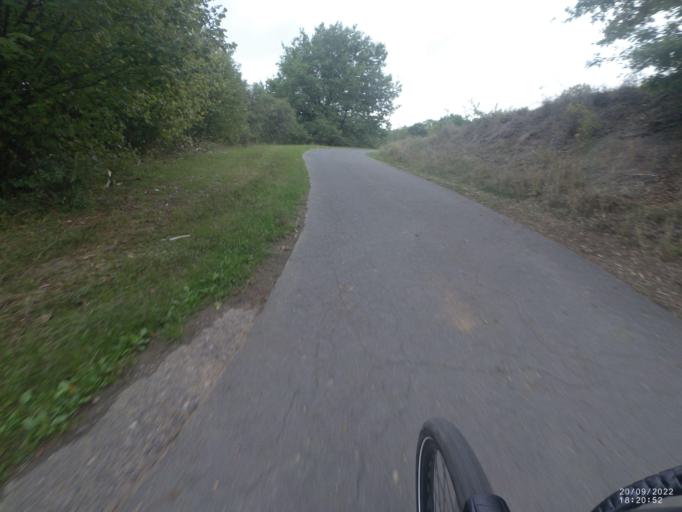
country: DE
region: Rheinland-Pfalz
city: Demerath
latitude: 50.1675
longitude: 6.9446
